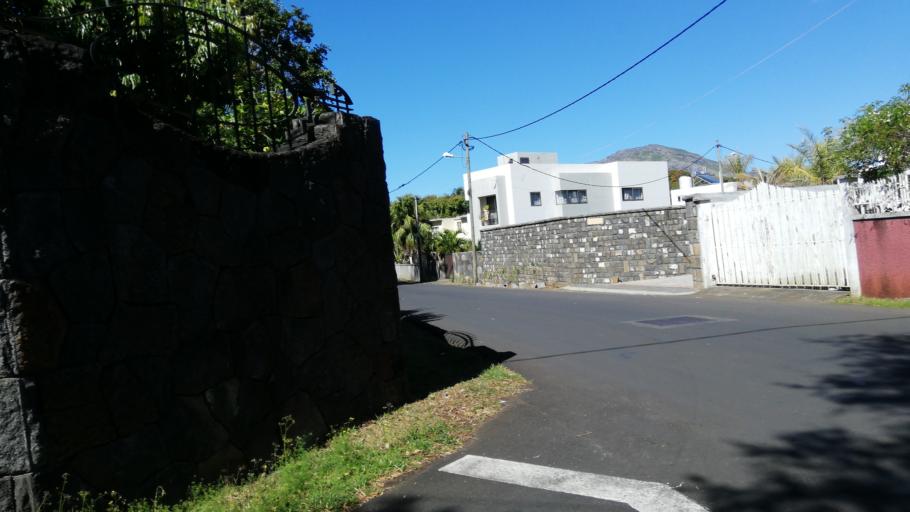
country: MU
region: Plaines Wilhems
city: Ebene
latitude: -20.2324
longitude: 57.4738
